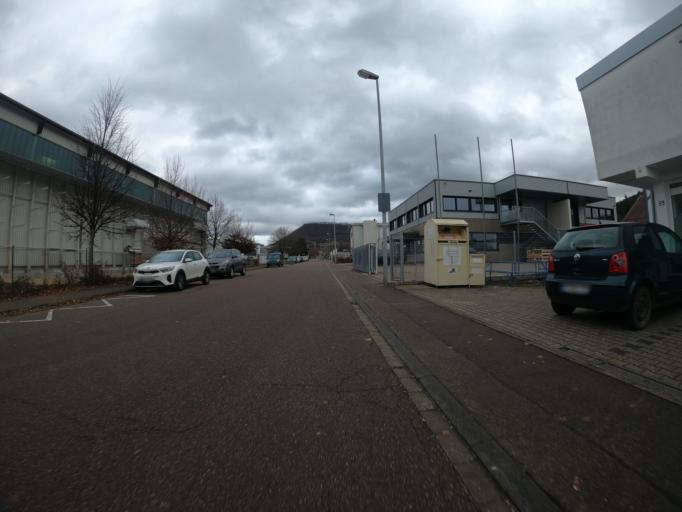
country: DE
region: Baden-Wuerttemberg
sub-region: Regierungsbezirk Stuttgart
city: Donzdorf
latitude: 48.6820
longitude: 9.7952
